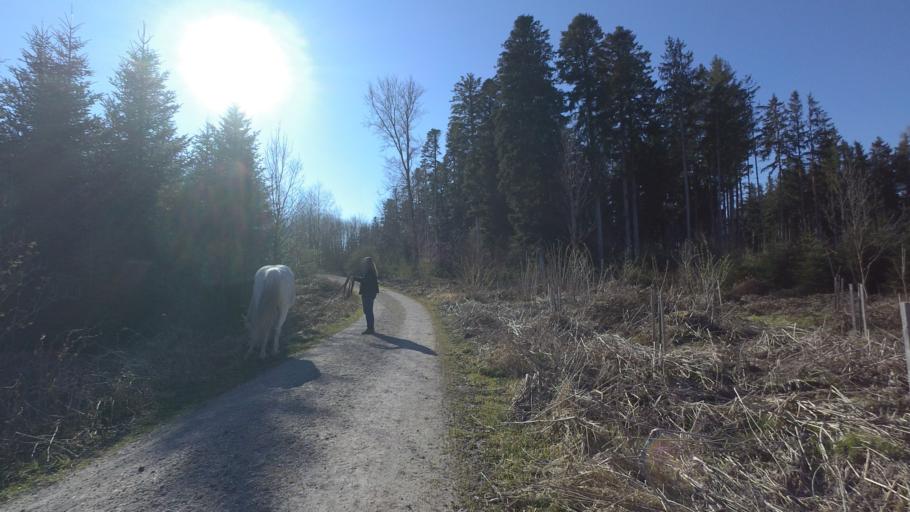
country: DE
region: Bavaria
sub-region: Upper Bavaria
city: Chieming
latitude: 47.9366
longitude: 12.5443
